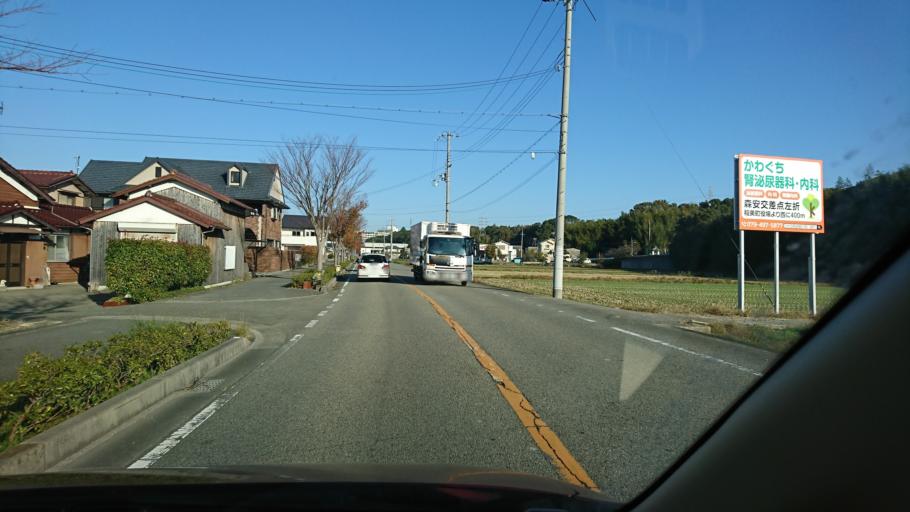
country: JP
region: Hyogo
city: Kakogawacho-honmachi
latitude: 34.7654
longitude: 134.8860
